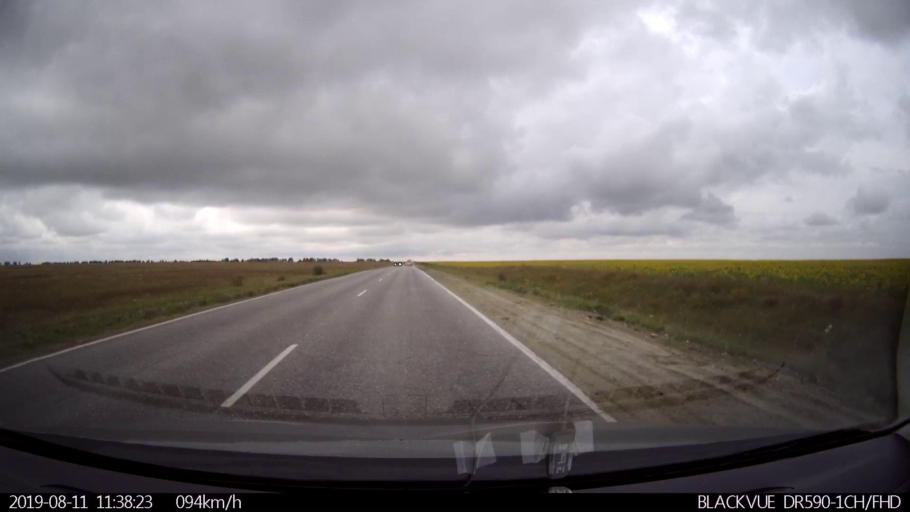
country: RU
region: Ulyanovsk
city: Silikatnyy
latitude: 53.9980
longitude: 48.1748
